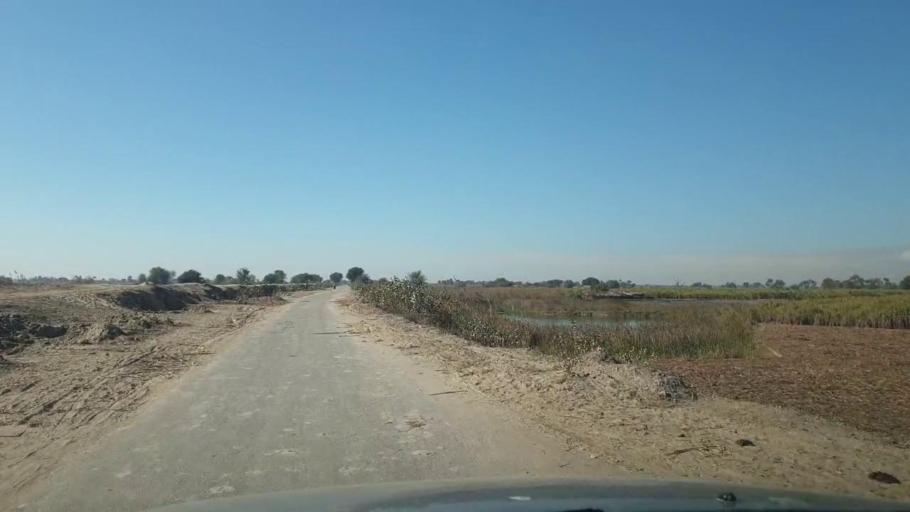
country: PK
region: Sindh
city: Ghotki
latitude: 28.0301
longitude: 69.2788
